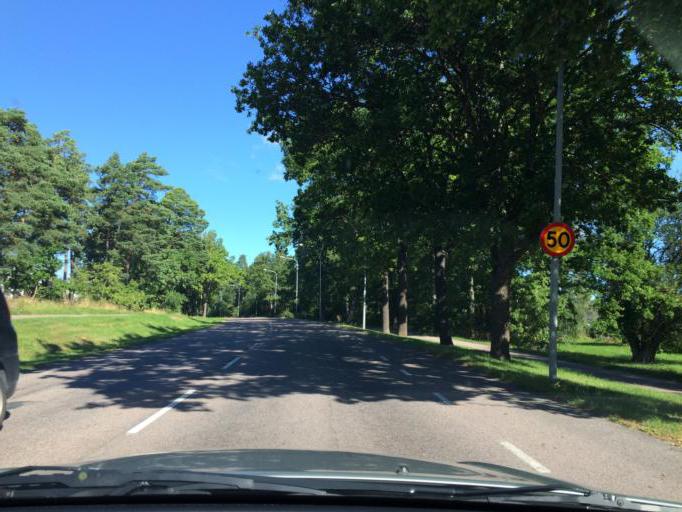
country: SE
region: Vaestmanland
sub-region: Vasteras
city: Vasteras
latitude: 59.5990
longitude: 16.5943
